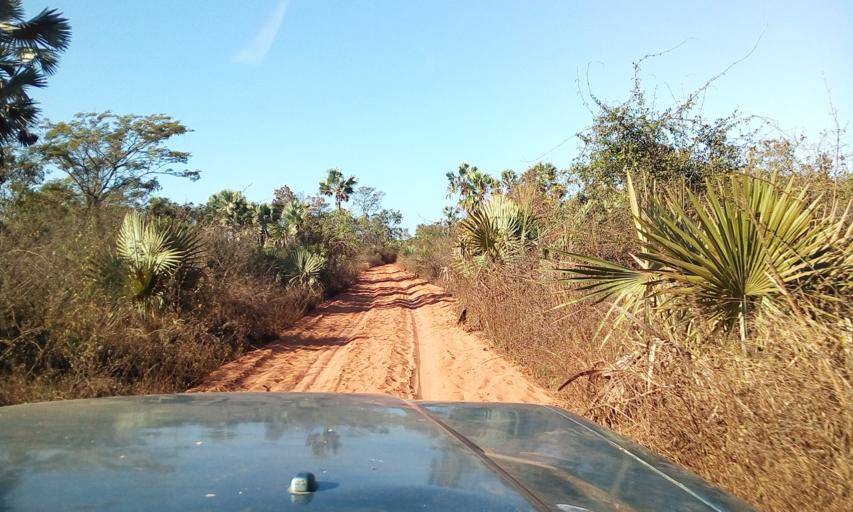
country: MG
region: Boeny
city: Sitampiky
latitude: -16.1902
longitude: 45.3620
